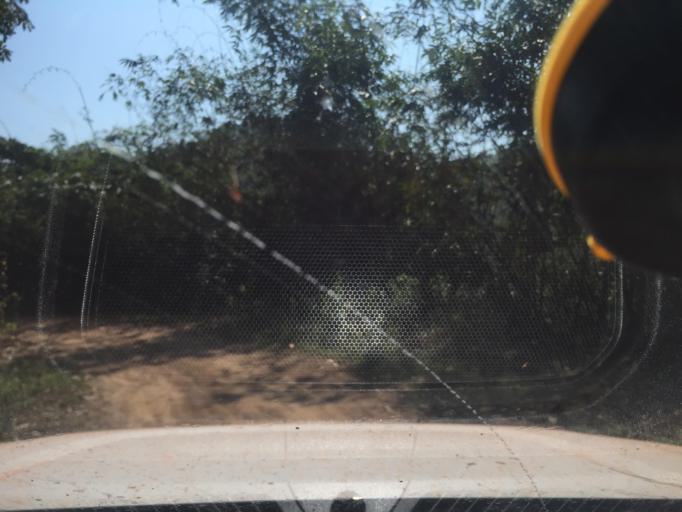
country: LA
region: Phongsali
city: Phongsali
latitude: 21.7027
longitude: 102.3898
